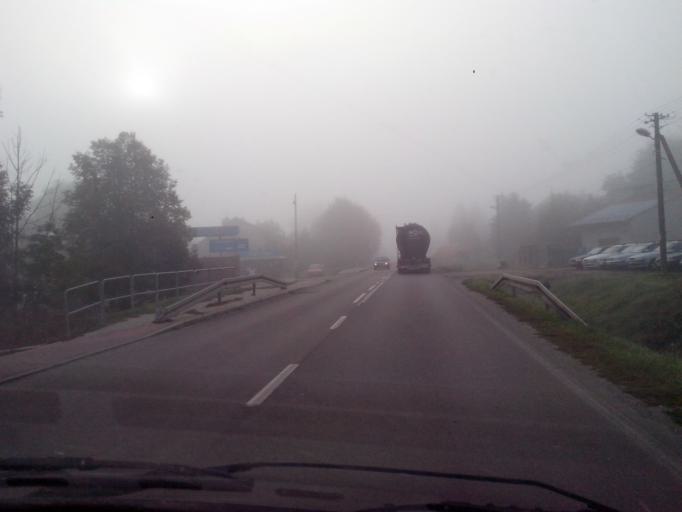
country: PL
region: Subcarpathian Voivodeship
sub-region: Przemysl
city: Przemysl
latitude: 49.7922
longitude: 22.7230
